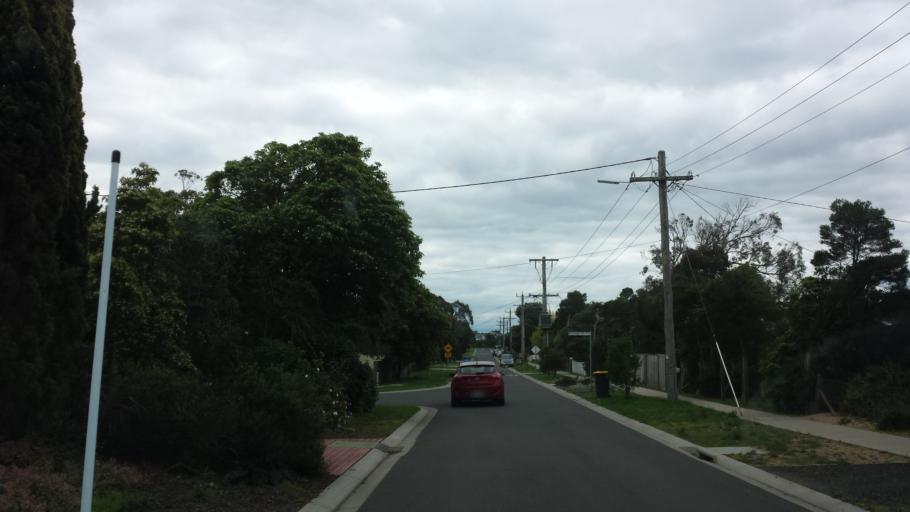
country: AU
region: Victoria
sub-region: Bass Coast
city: Cowes
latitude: -38.4591
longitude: 145.2146
